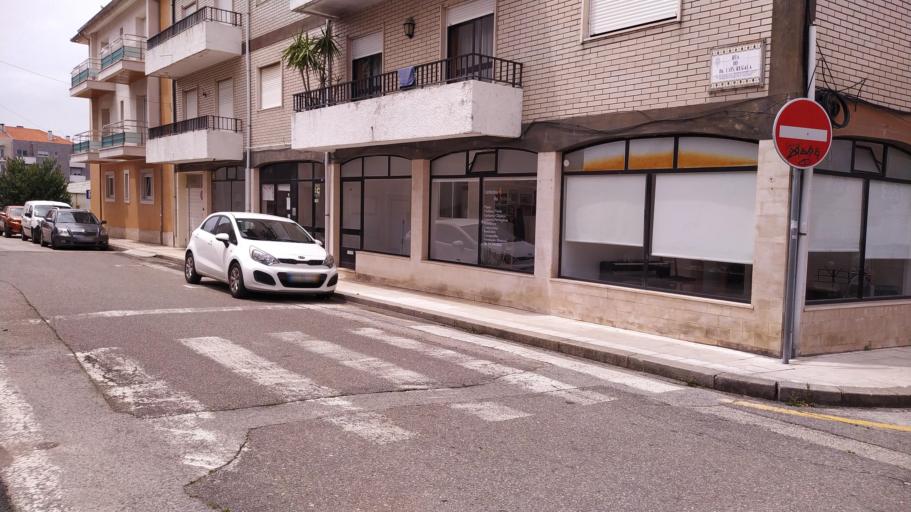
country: PT
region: Aveiro
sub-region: Aveiro
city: Aveiro
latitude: 40.6453
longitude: -8.6491
